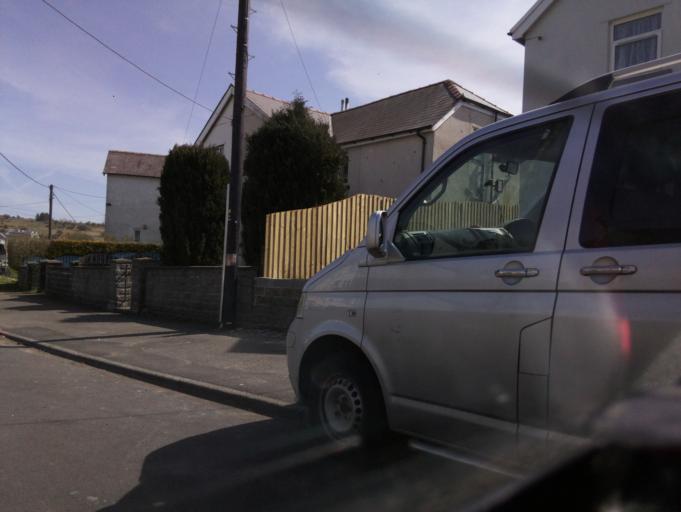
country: GB
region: Wales
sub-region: Merthyr Tydfil County Borough
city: Merthyr Tydfil
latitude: 51.7719
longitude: -3.3593
